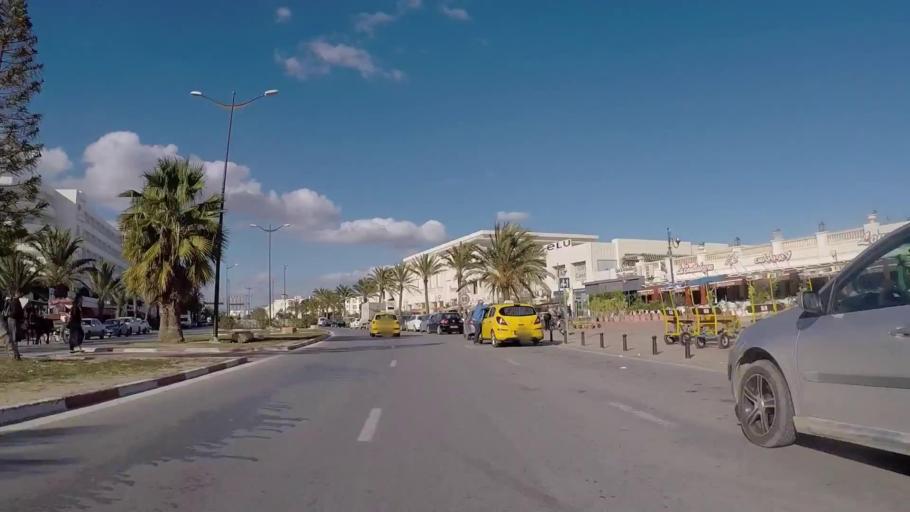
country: TN
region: Nabul
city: Al Hammamat
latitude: 36.3708
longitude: 10.5414
